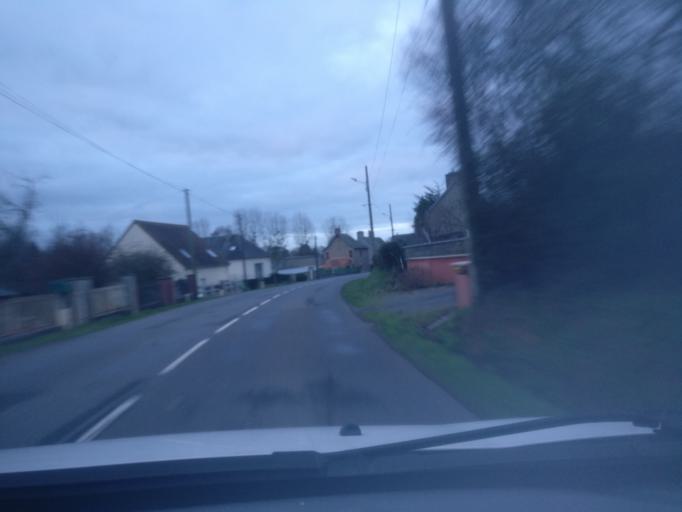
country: FR
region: Lower Normandy
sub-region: Departement de la Manche
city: Marcey-les-Greves
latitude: 48.6838
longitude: -1.3844
